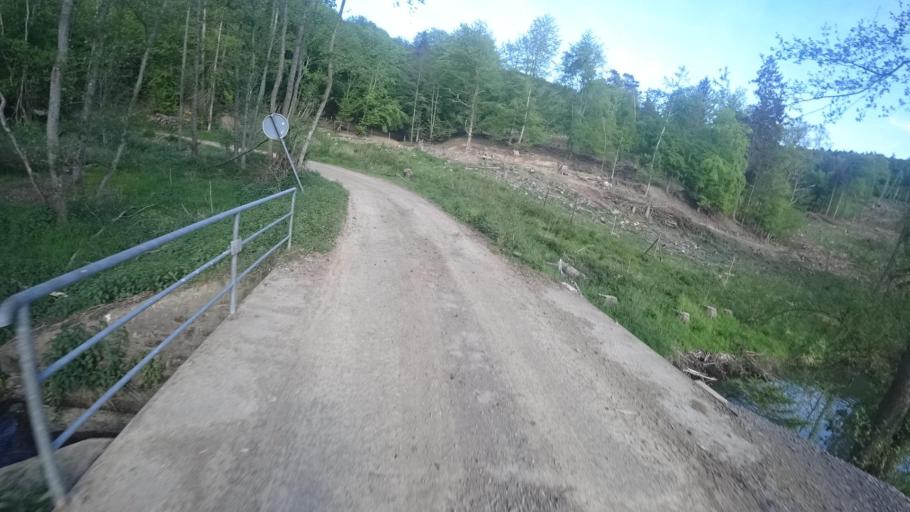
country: DE
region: Rheinland-Pfalz
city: Altenahr
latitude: 50.5328
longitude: 6.9728
